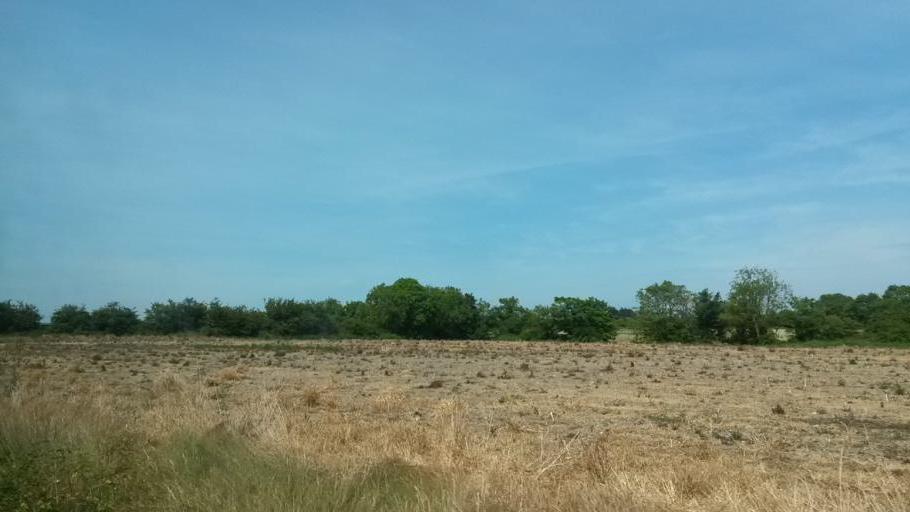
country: IE
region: Leinster
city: Lusk
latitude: 53.5099
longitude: -6.1508
